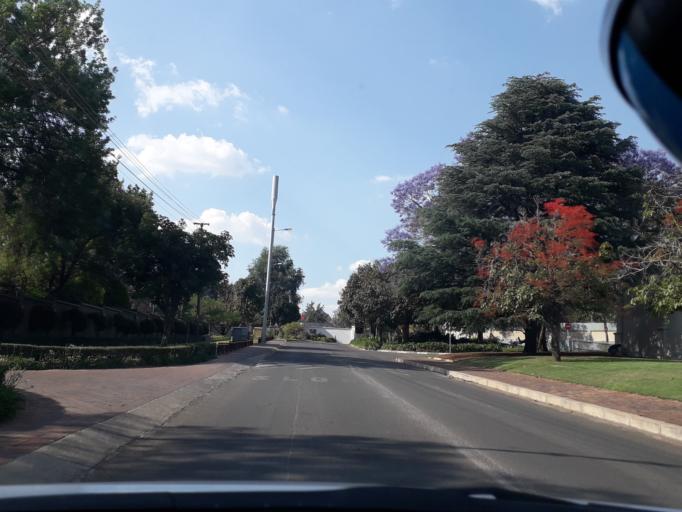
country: ZA
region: Gauteng
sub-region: City of Johannesburg Metropolitan Municipality
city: Johannesburg
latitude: -26.1174
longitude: 28.0371
